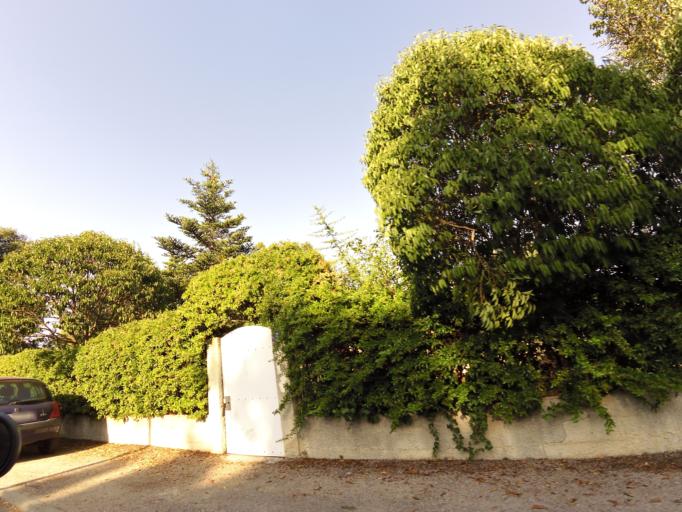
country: FR
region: Languedoc-Roussillon
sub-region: Departement de l'Herault
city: Villetelle
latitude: 43.7272
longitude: 4.1146
